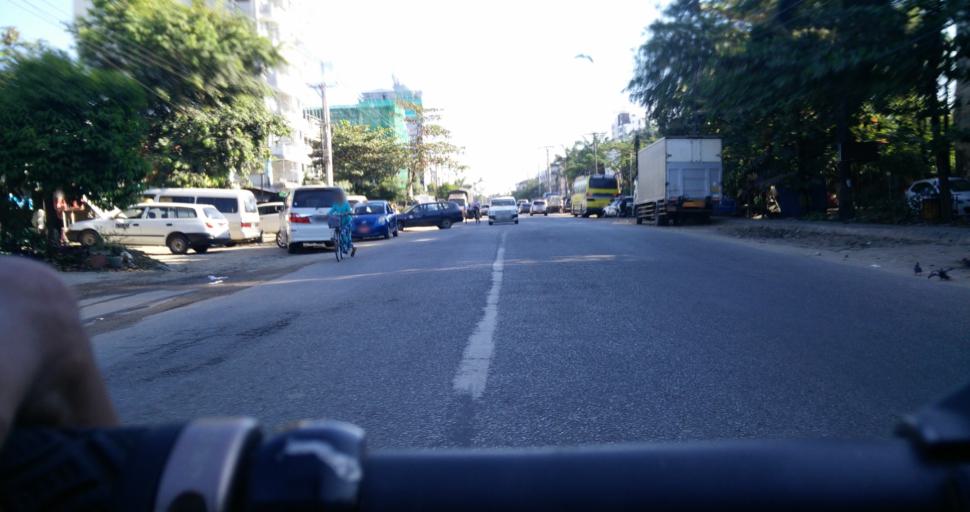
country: MM
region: Yangon
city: Yangon
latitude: 16.8425
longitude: 96.1972
